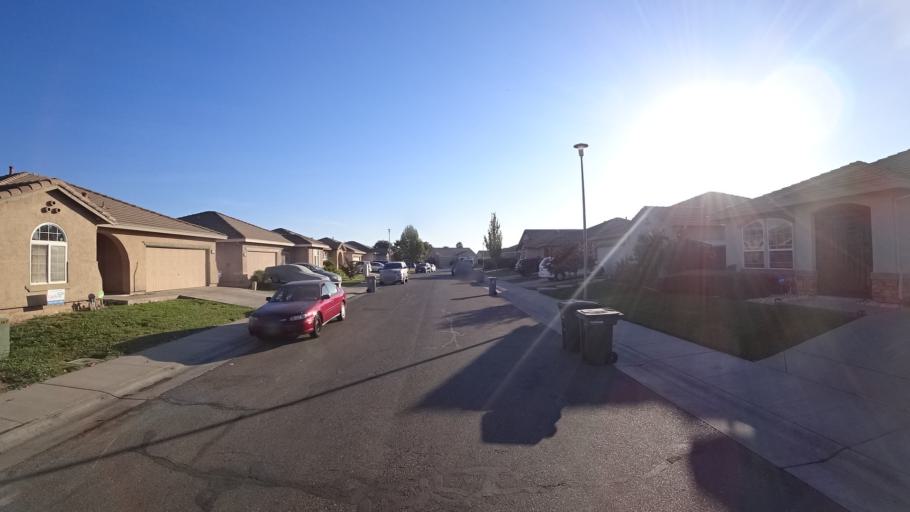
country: US
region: California
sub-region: Sacramento County
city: Parkway
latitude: 38.4759
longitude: -121.4934
